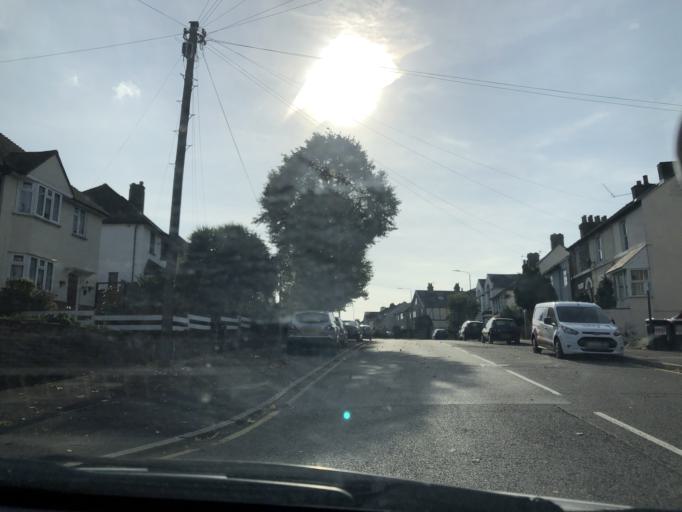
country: GB
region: England
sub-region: Greater London
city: Bexley
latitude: 51.4478
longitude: 0.1808
